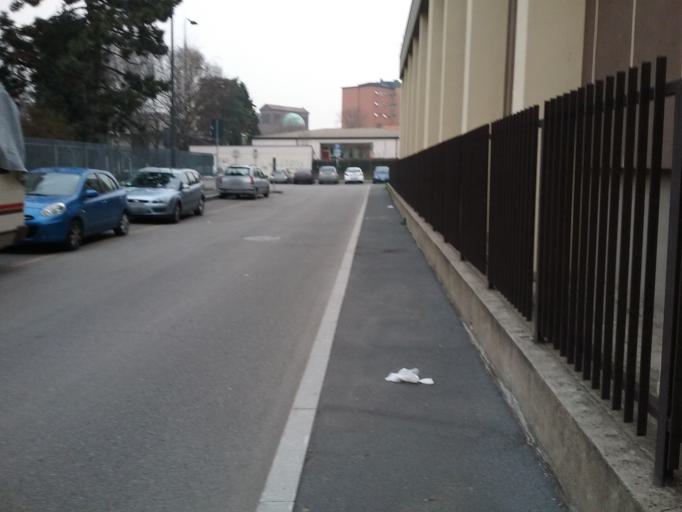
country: IT
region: Lombardy
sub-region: Citta metropolitana di Milano
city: Cesano Boscone
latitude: 45.4731
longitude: 9.1129
